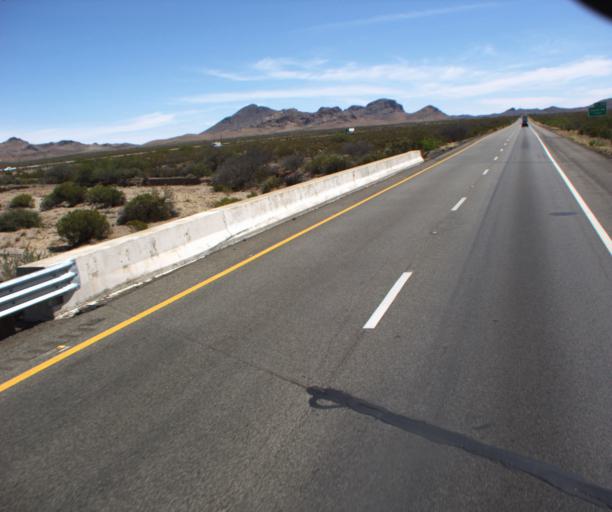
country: US
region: New Mexico
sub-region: Hidalgo County
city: Lordsburg
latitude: 32.2343
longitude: -109.0785
